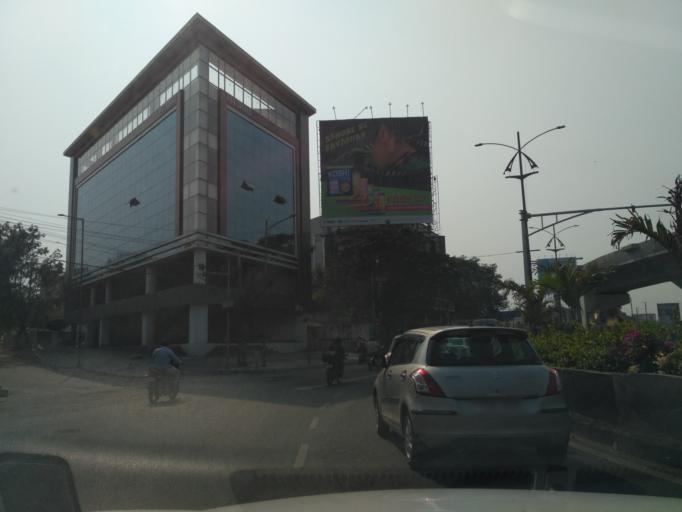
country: IN
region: Telangana
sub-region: Rangareddi
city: Kukatpalli
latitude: 17.4384
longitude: 78.3988
